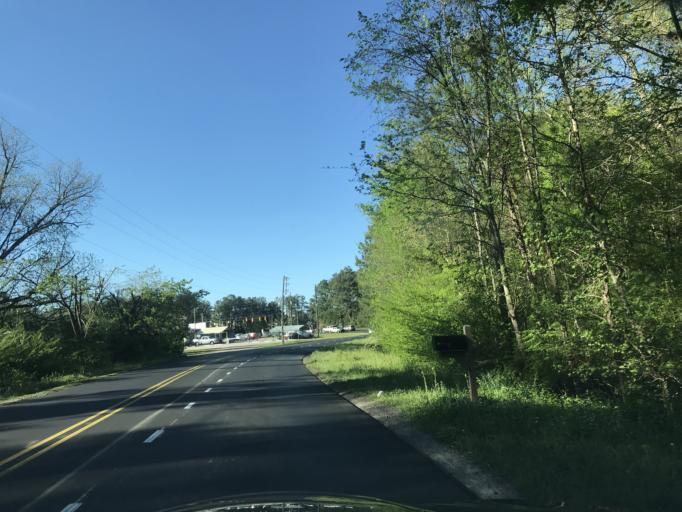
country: US
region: North Carolina
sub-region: Wake County
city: Knightdale
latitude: 35.8541
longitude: -78.5552
